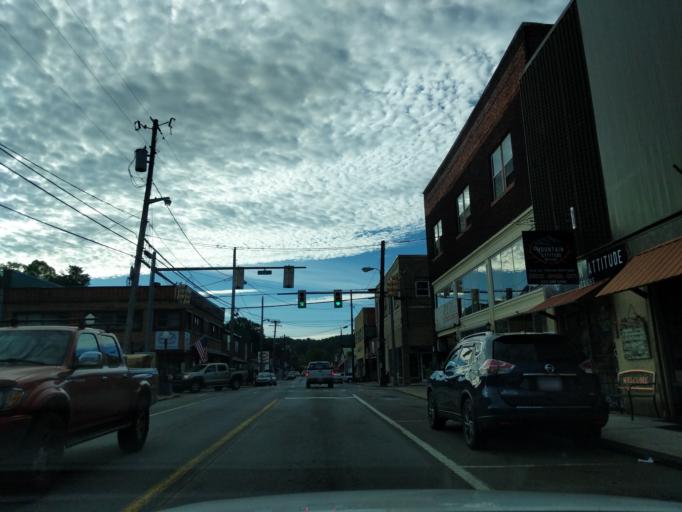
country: US
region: Georgia
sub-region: Fannin County
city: McCaysville
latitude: 34.9887
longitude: -84.3709
